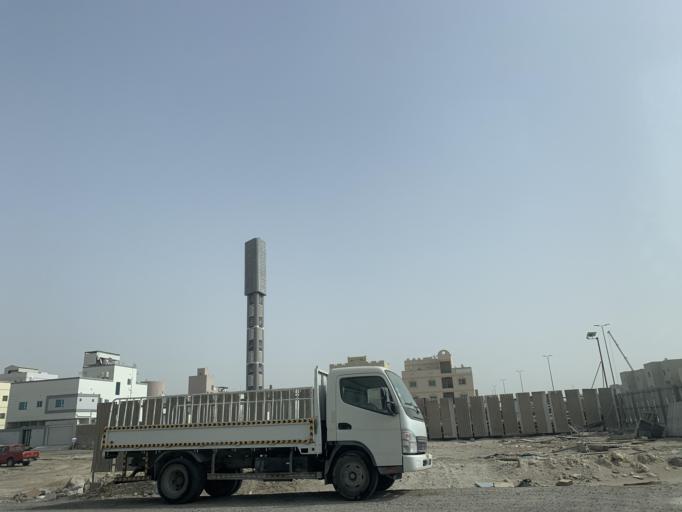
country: BH
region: Northern
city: Madinat `Isa
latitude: 26.1806
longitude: 50.5209
